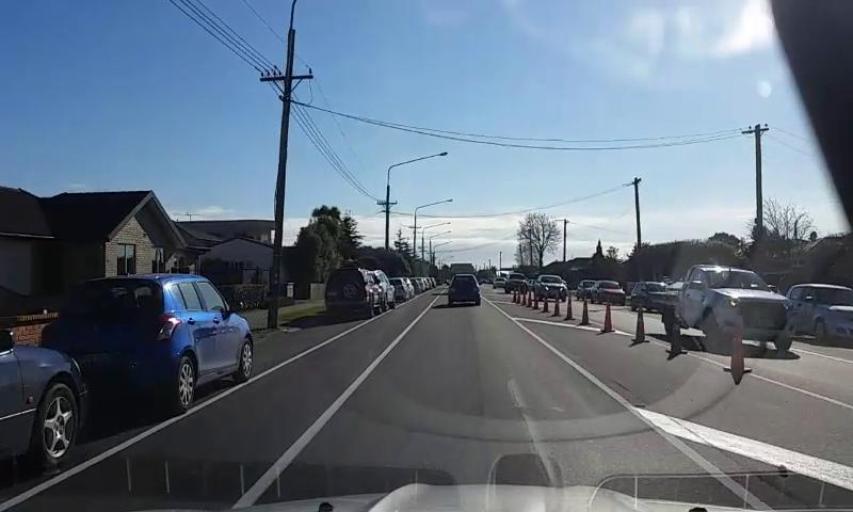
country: NZ
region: Canterbury
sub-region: Christchurch City
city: Christchurch
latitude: -43.5051
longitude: 172.6625
